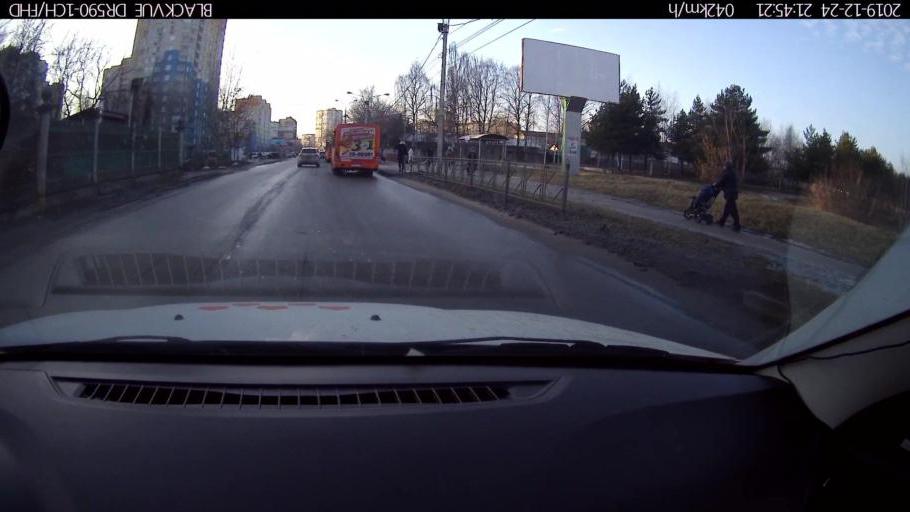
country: RU
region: Nizjnij Novgorod
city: Gorbatovka
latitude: 56.2400
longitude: 43.8438
